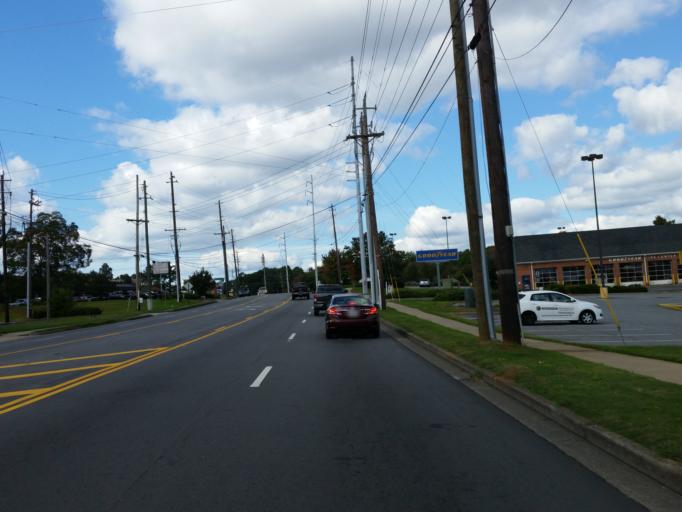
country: US
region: Georgia
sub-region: Cobb County
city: Vinings
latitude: 33.9204
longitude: -84.4673
